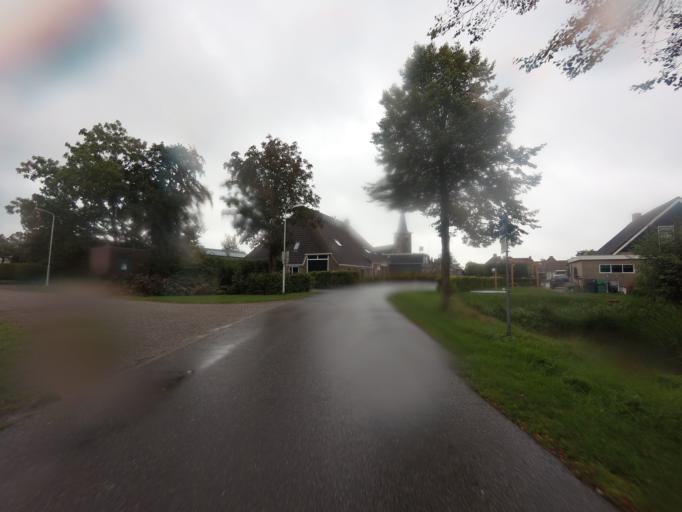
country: NL
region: Friesland
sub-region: Gemeente Tytsjerksteradiel
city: Garyp
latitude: 53.1321
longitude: 5.9415
